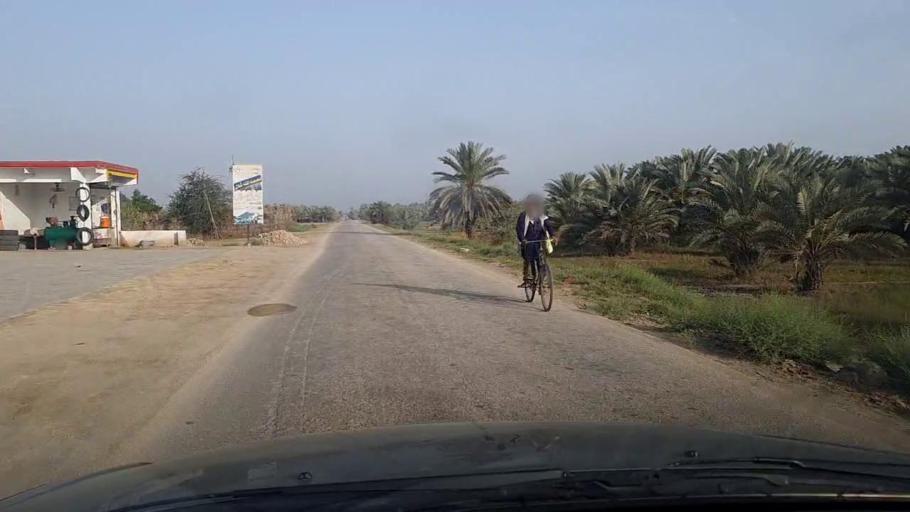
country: PK
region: Sindh
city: Khairpur
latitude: 27.5401
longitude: 68.7091
